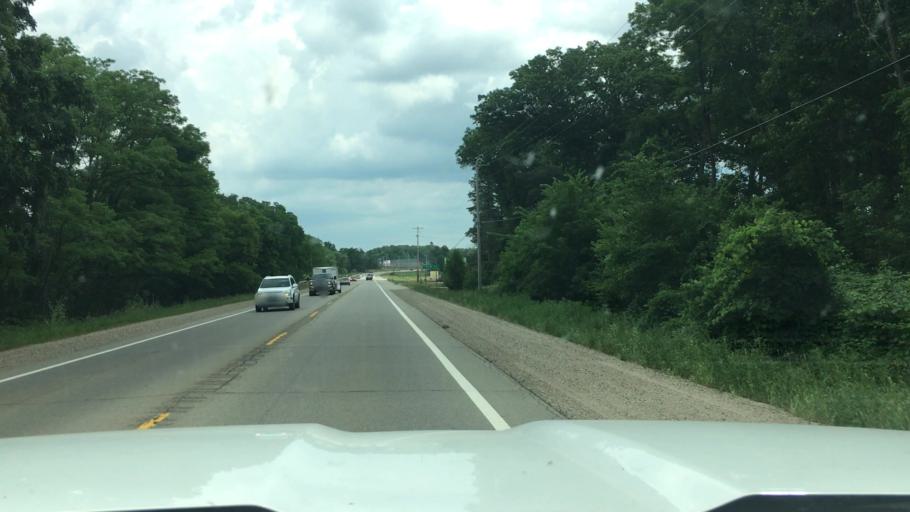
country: US
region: Michigan
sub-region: Montcalm County
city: Greenville
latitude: 43.1763
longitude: -85.3668
